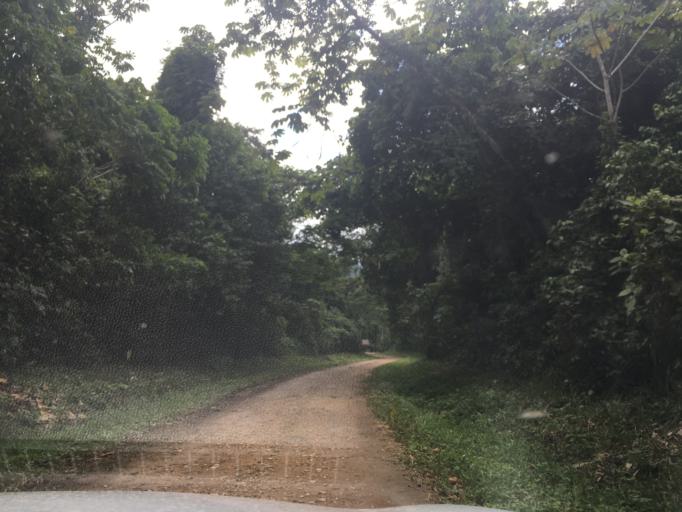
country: BZ
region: Stann Creek
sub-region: Dangriga
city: Dangriga
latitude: 16.9315
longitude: -88.3847
